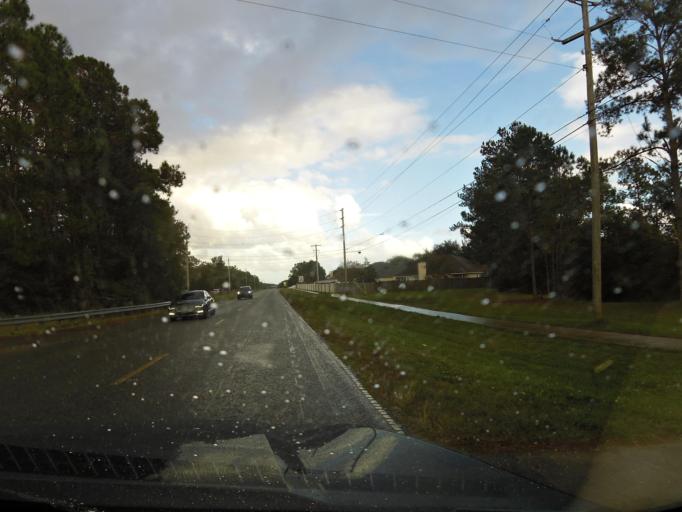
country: US
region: Florida
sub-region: Clay County
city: Asbury Lake
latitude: 30.0462
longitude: -81.7979
